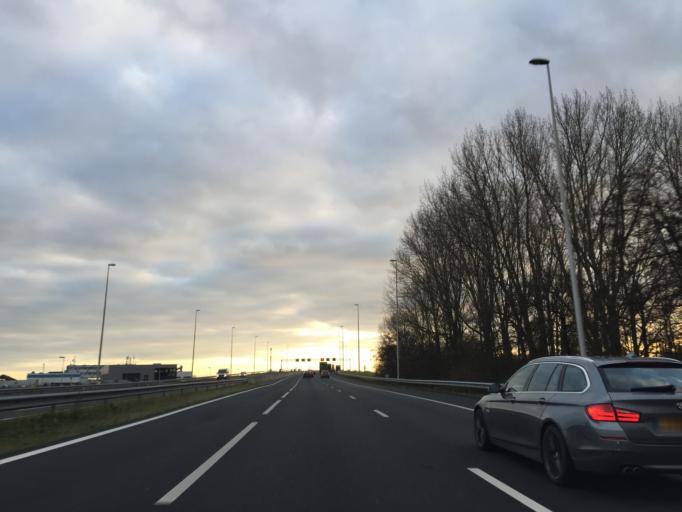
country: NL
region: South Holland
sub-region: Gemeente Lansingerland
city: Bleiswijk
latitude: 52.0284
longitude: 4.5724
